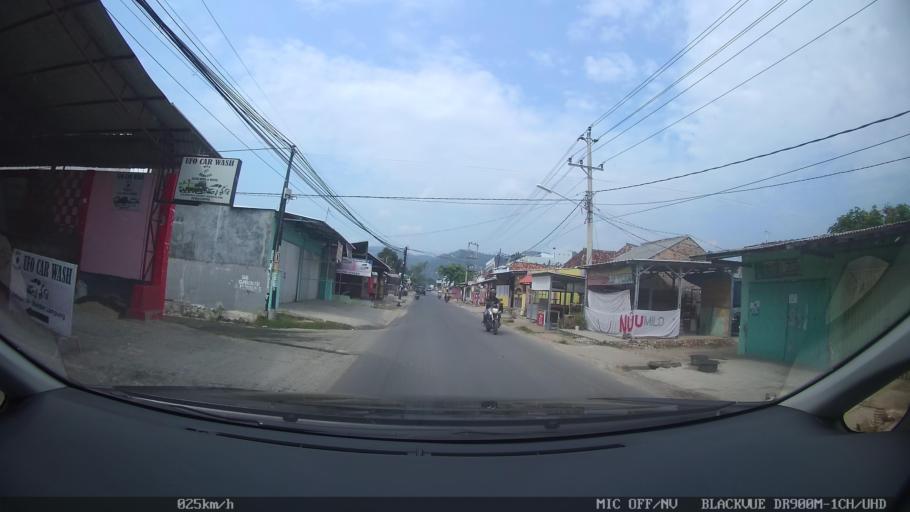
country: ID
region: Lampung
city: Bandarlampung
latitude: -5.4602
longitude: 105.2514
